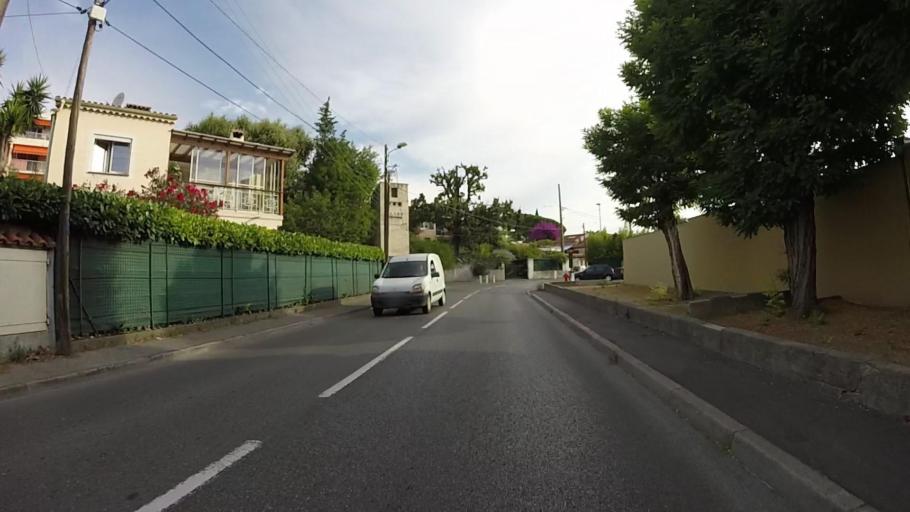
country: FR
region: Provence-Alpes-Cote d'Azur
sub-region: Departement des Alpes-Maritimes
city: Antibes
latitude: 43.5884
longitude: 7.1063
